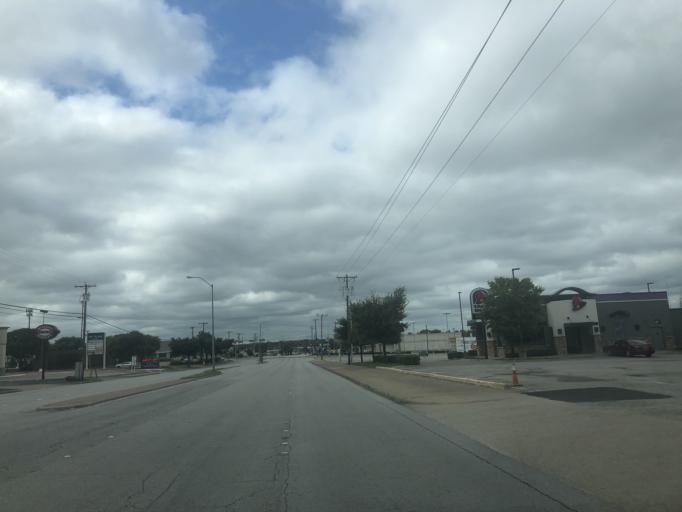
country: US
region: Texas
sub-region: Dallas County
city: Duncanville
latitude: 32.6495
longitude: -96.9257
